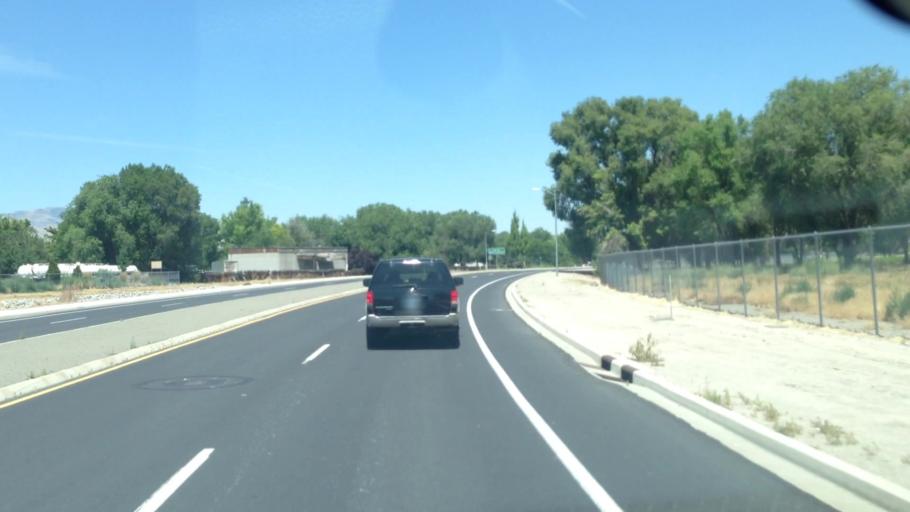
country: US
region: Nevada
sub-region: Washoe County
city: Sparks
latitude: 39.4847
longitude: -119.7751
